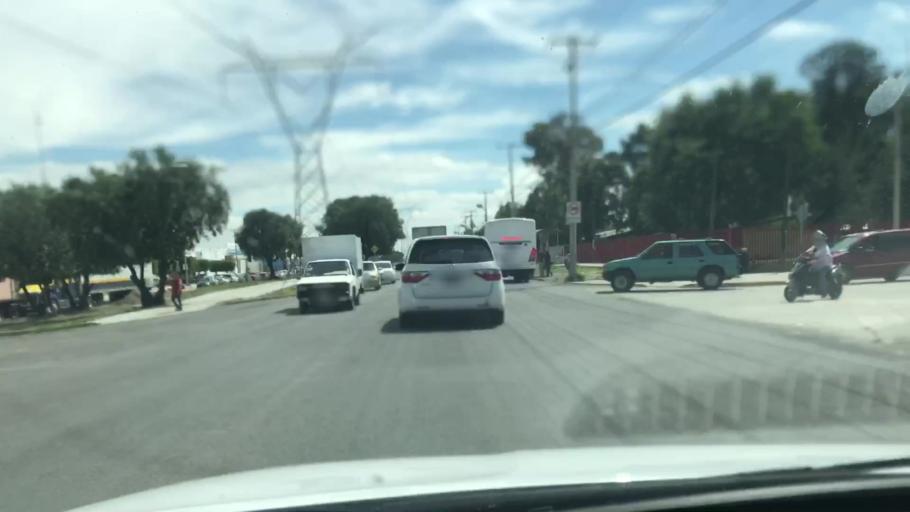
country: MX
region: Guanajuato
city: Celaya
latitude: 20.5518
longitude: -100.8163
